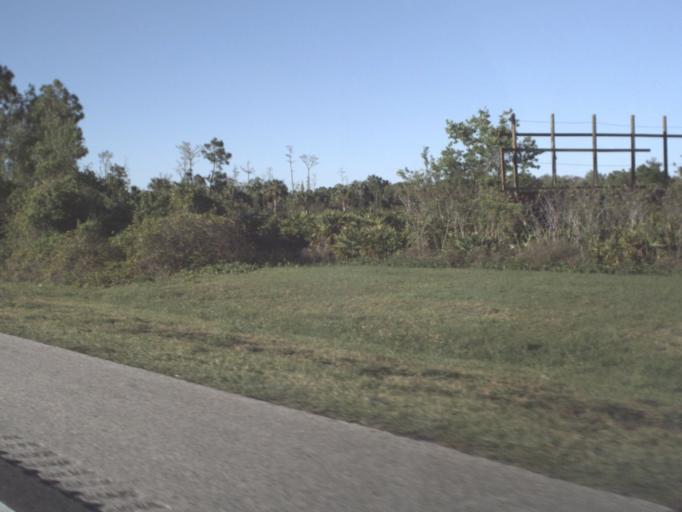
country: US
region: Florida
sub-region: Flagler County
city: Flagler Beach
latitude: 29.4220
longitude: -81.1630
